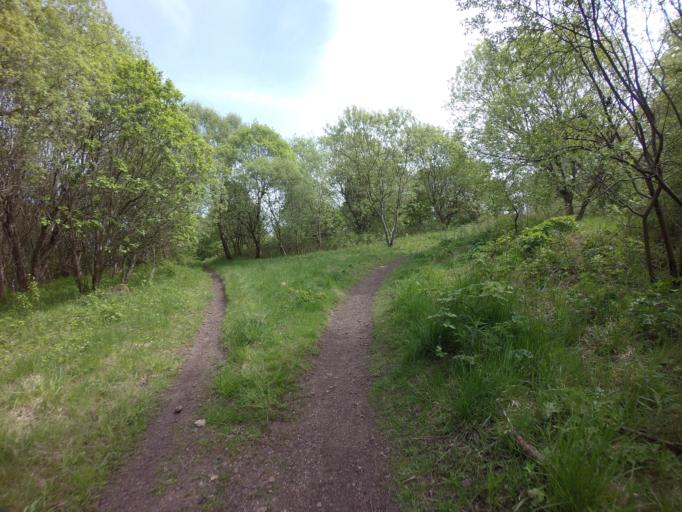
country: GB
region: Scotland
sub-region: West Lothian
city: Mid Calder
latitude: 55.9109
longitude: -3.4876
